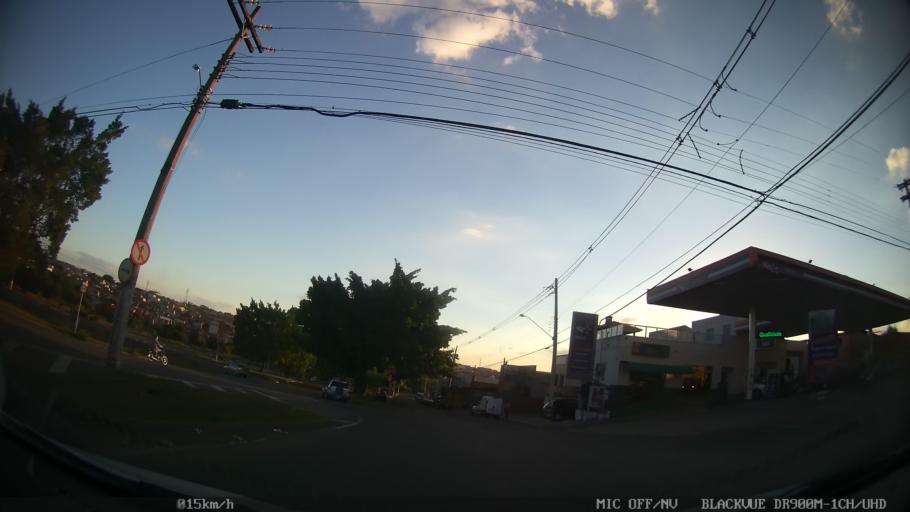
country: BR
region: Sao Paulo
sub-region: Santa Barbara D'Oeste
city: Santa Barbara d'Oeste
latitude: -22.7348
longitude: -47.3912
